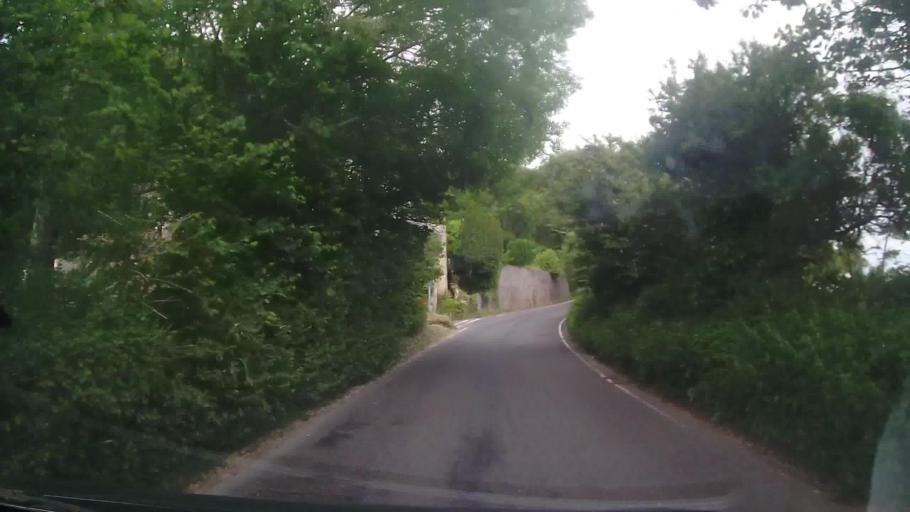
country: GB
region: England
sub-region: Devon
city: Dartmouth
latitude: 50.3198
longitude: -3.6132
